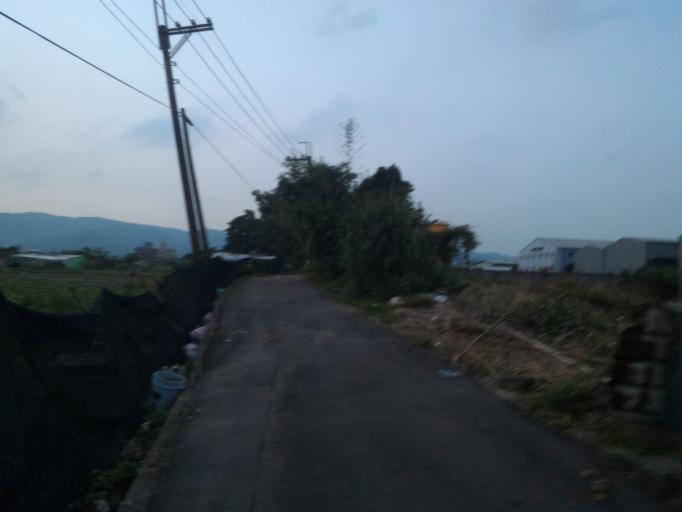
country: TW
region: Taipei
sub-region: Taipei
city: Banqiao
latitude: 24.9551
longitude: 121.4035
